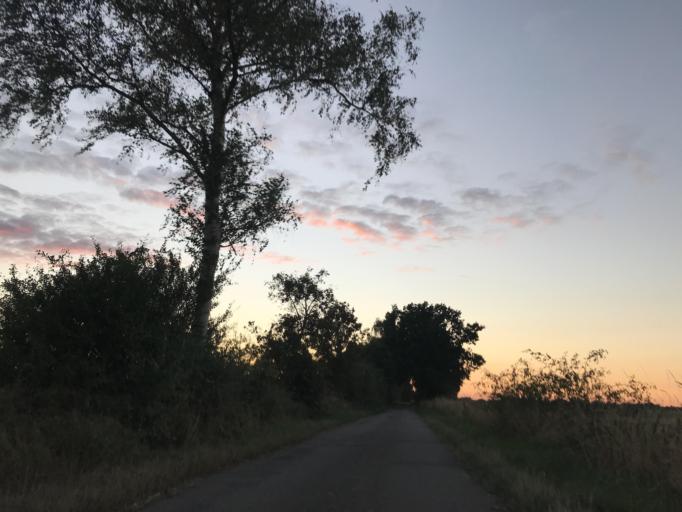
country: DE
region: Lower Saxony
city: Reinstorf
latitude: 53.2261
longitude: 10.5987
